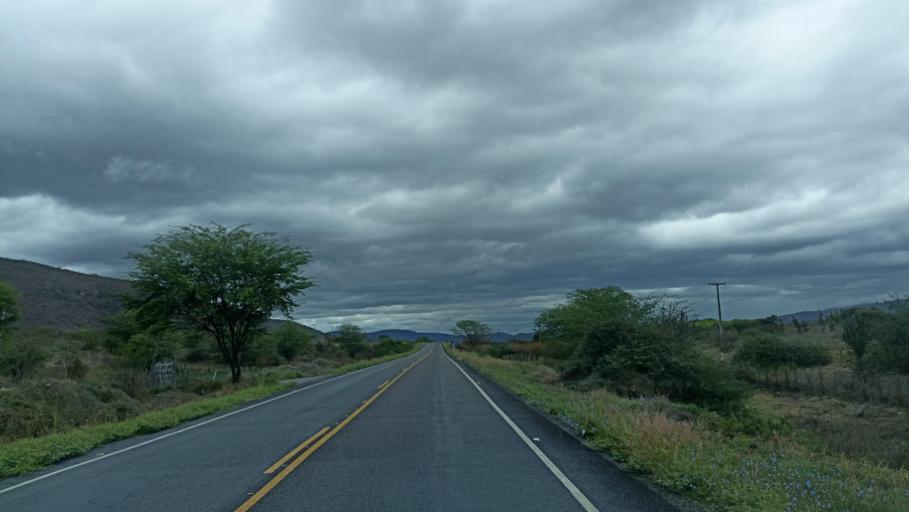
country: BR
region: Bahia
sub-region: Iacu
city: Iacu
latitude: -12.8783
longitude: -40.3888
